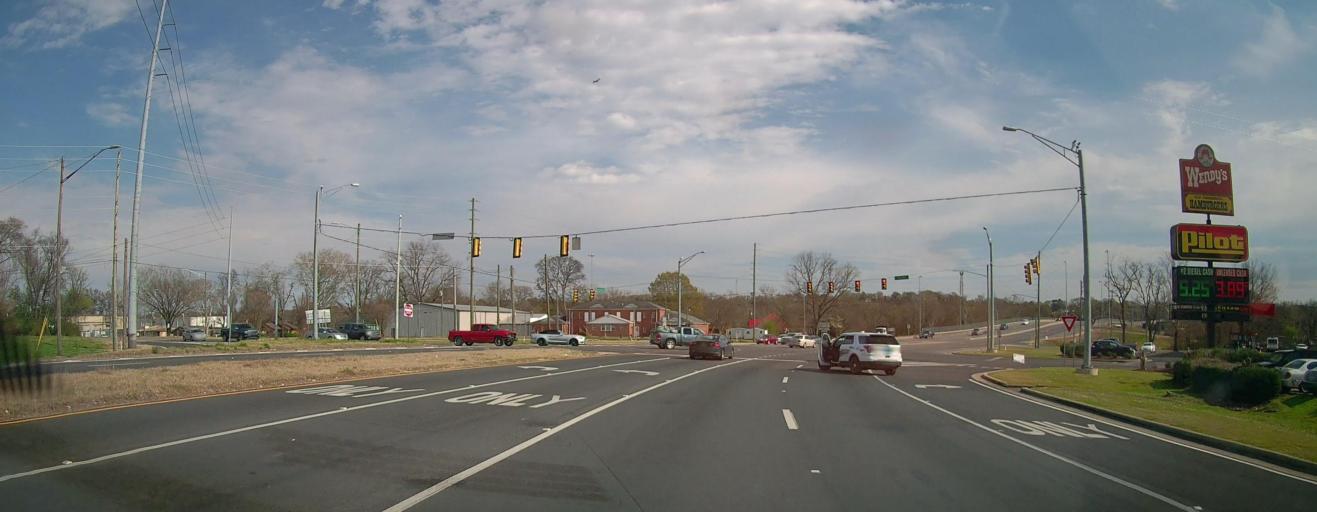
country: US
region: Alabama
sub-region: Jefferson County
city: Birmingham
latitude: 33.5304
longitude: -86.8513
